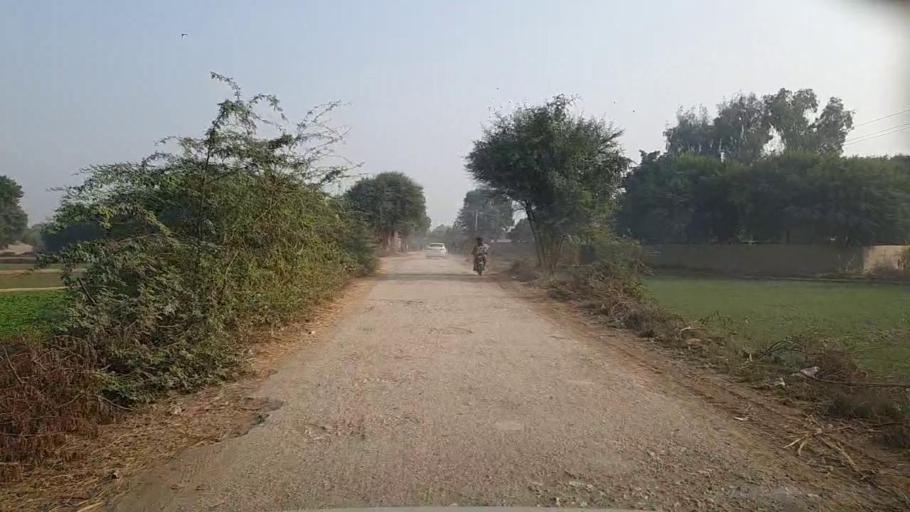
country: PK
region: Sindh
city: Kandiari
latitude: 27.0339
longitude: 68.4842
